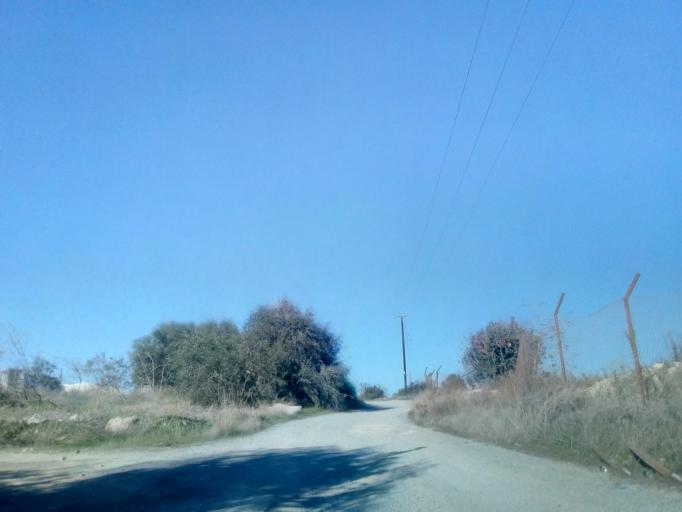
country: CY
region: Limassol
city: Ypsonas
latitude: 34.6773
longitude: 32.9738
